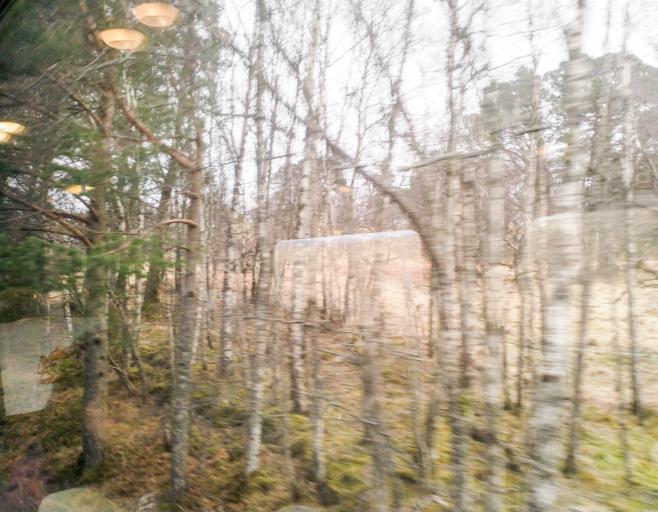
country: GB
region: Scotland
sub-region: Highland
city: Spean Bridge
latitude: 56.5729
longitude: -4.6868
